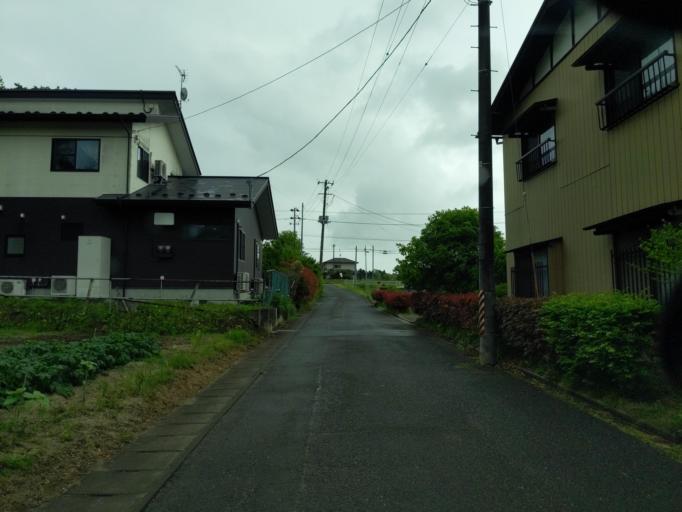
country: JP
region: Fukushima
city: Koriyama
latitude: 37.3425
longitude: 140.3893
